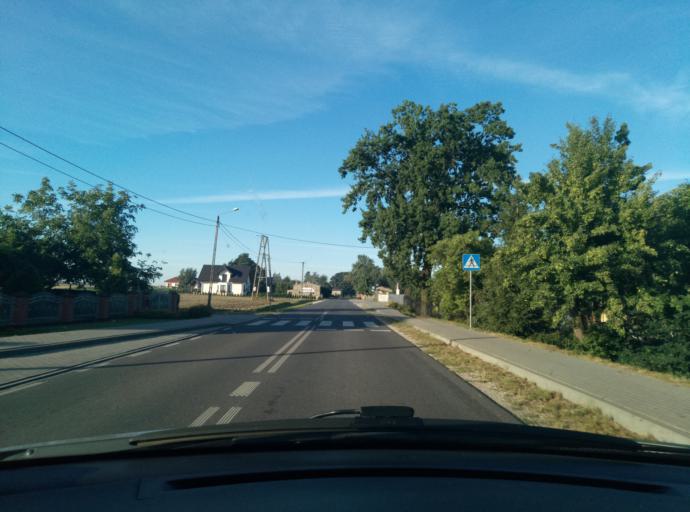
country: PL
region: Kujawsko-Pomorskie
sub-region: Powiat golubsko-dobrzynski
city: Kowalewo Pomorskie
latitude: 53.2013
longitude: 18.9163
